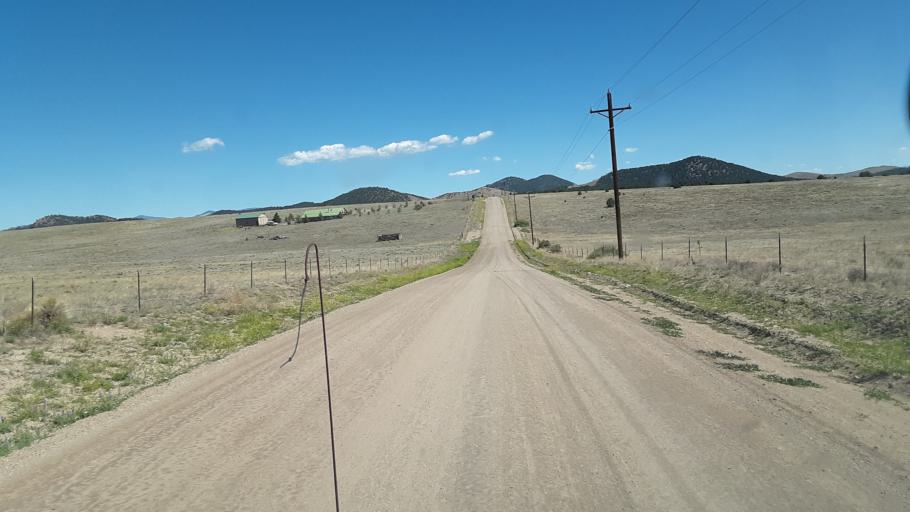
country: US
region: Colorado
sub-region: Custer County
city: Westcliffe
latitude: 38.2780
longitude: -105.5009
